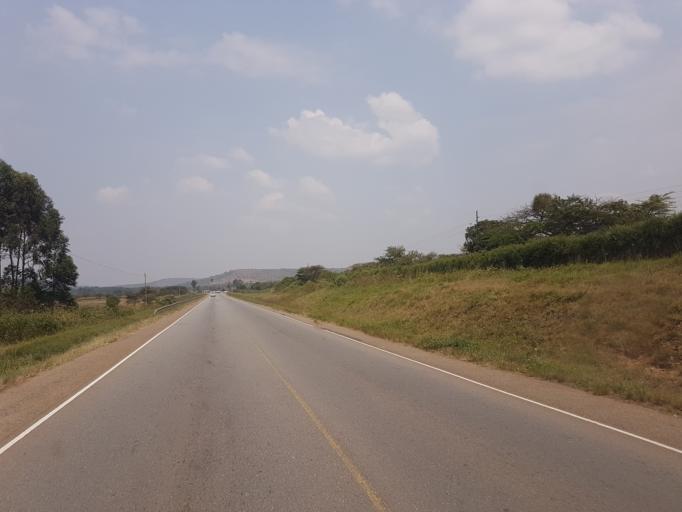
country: UG
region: Western Region
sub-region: Mbarara District
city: Mbarara
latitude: -0.4896
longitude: 30.8748
